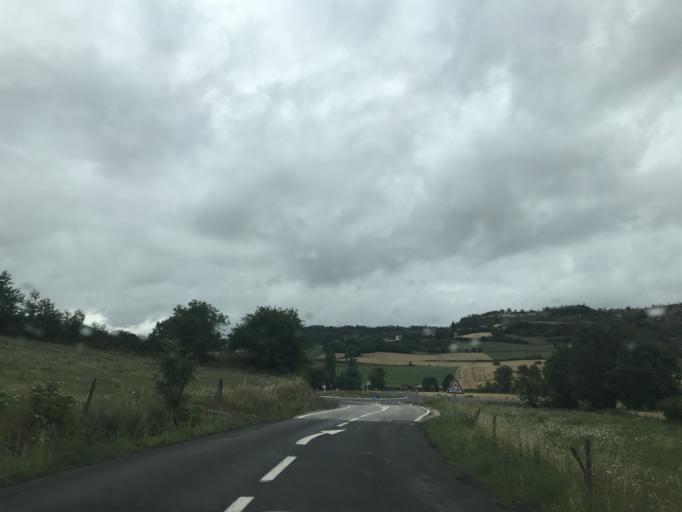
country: FR
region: Auvergne
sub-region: Departement de la Haute-Loire
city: Polignac
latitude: 45.0610
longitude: 3.8693
